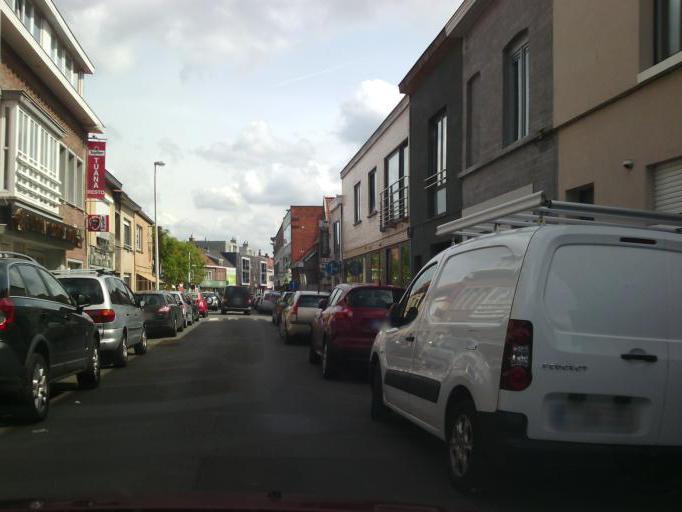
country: BE
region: Flanders
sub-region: Provincie Oost-Vlaanderen
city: Evergem
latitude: 51.0725
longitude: 3.6793
